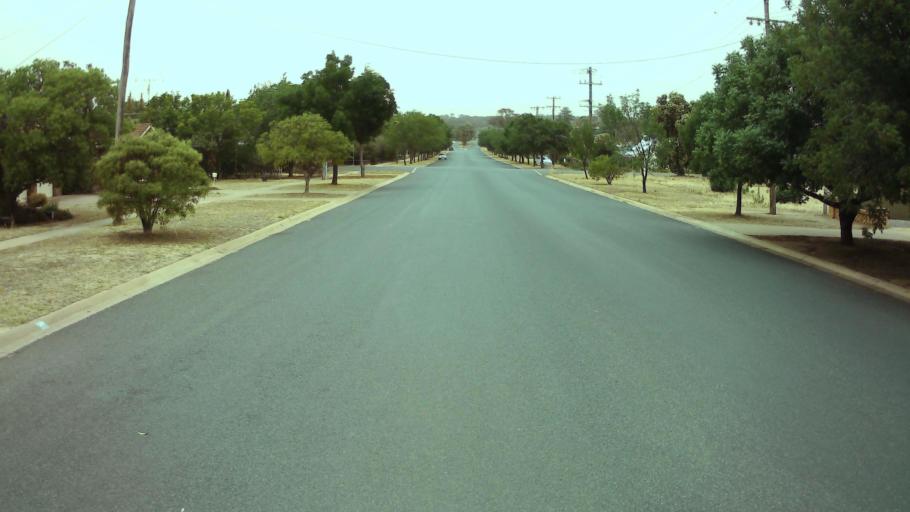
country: AU
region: New South Wales
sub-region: Weddin
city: Grenfell
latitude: -33.8989
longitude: 148.1650
